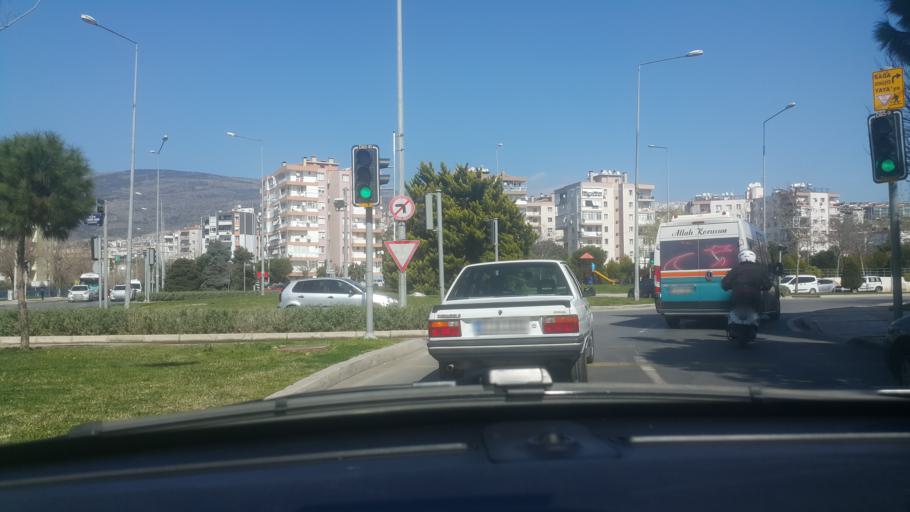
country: TR
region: Izmir
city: Bornova
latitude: 38.4658
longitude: 27.1949
